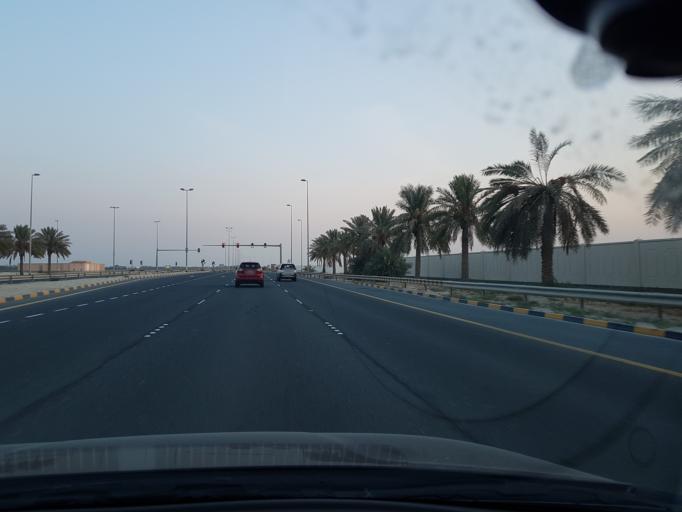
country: BH
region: Central Governorate
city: Dar Kulayb
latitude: 26.0397
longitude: 50.4998
